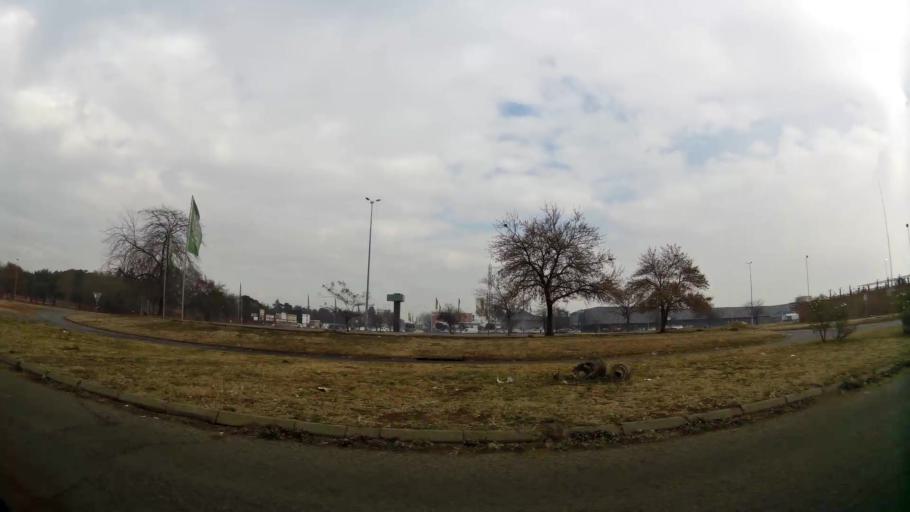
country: ZA
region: Gauteng
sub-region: Sedibeng District Municipality
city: Vanderbijlpark
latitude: -26.7024
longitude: 27.8407
